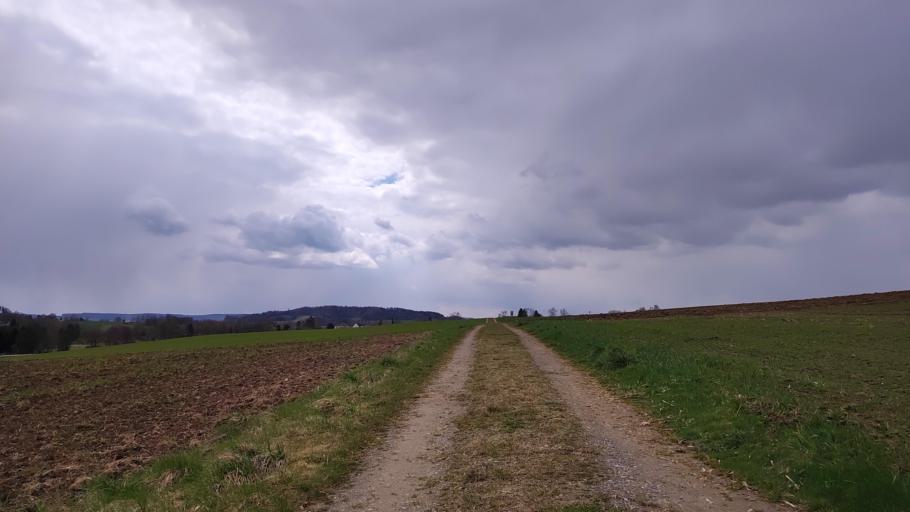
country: DE
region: Bavaria
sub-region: Swabia
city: Dinkelscherben
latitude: 48.3695
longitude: 10.5680
